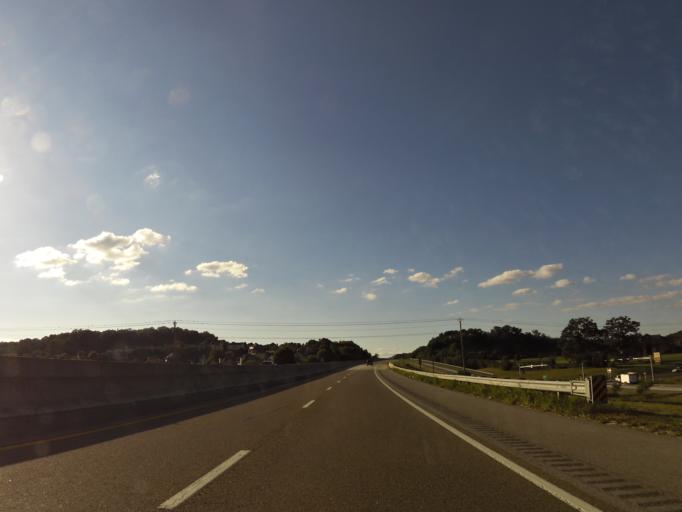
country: US
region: Tennessee
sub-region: Knox County
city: Farragut
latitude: 35.8756
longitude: -84.0936
